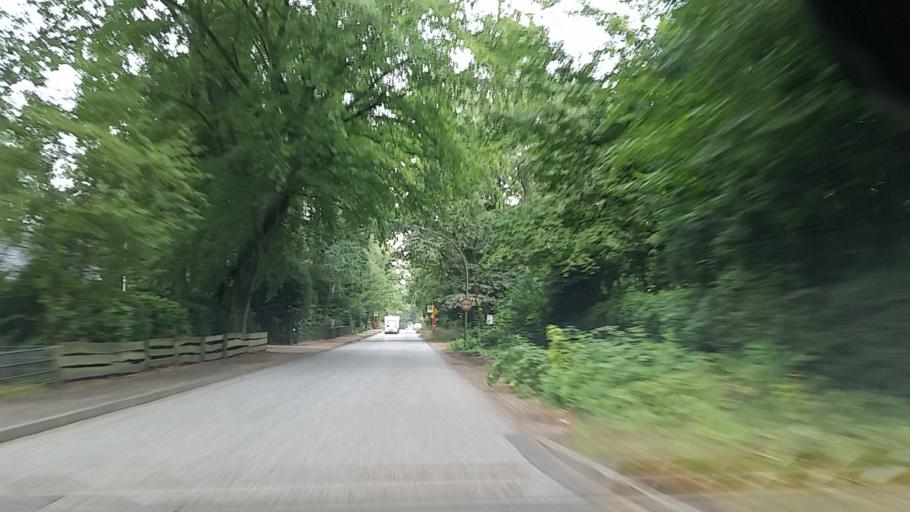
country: DE
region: Schleswig-Holstein
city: Wedel
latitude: 53.5714
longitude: 9.7528
